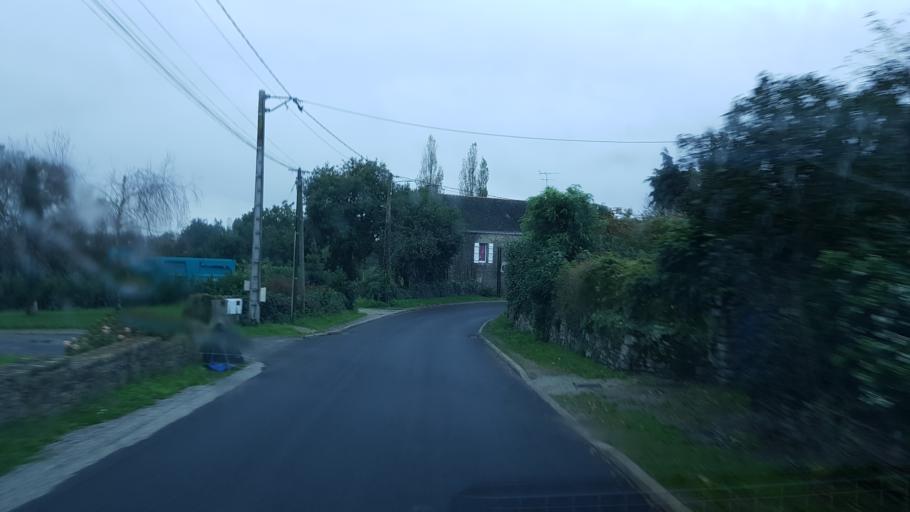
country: FR
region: Brittany
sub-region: Departement du Morbihan
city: Trefflean
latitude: 47.6619
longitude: -2.6217
